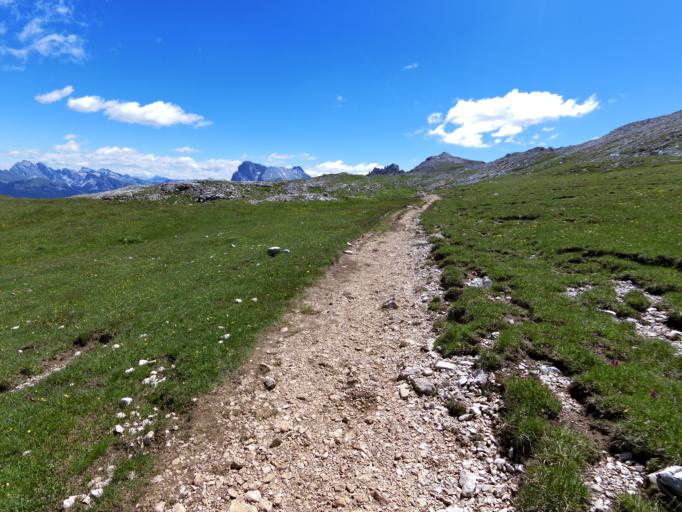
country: IT
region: Trentino-Alto Adige
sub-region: Bolzano
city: Siusi
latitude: 46.5051
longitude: 11.5915
